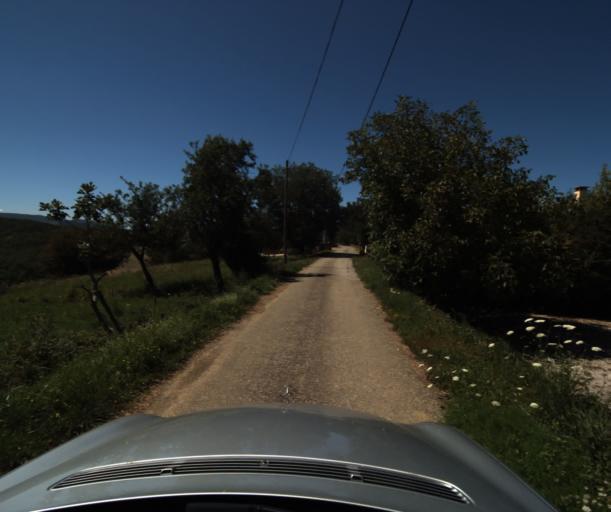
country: FR
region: Midi-Pyrenees
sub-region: Departement de l'Ariege
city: Belesta
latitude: 42.9624
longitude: 1.9289
